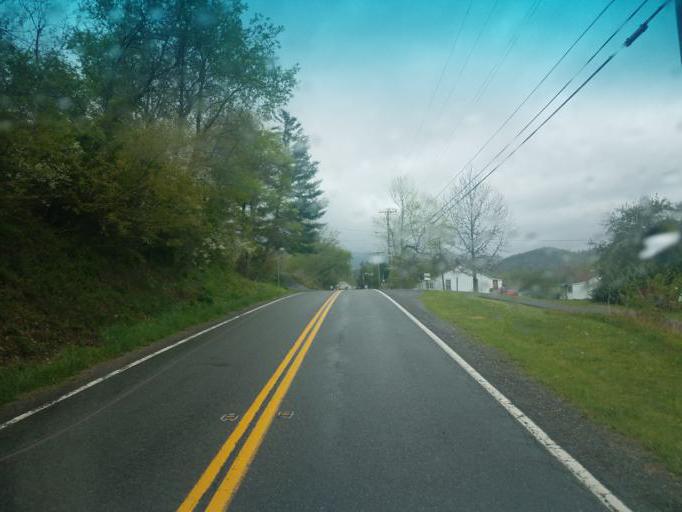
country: US
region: Virginia
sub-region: Bland County
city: Bland
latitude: 37.1651
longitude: -81.1468
